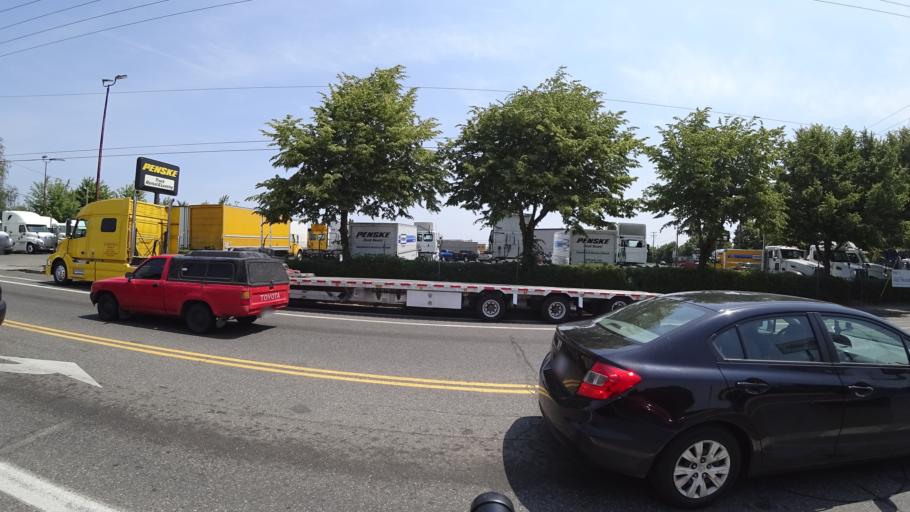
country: US
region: Washington
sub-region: Clark County
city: Vancouver
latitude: 45.5833
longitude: -122.6679
